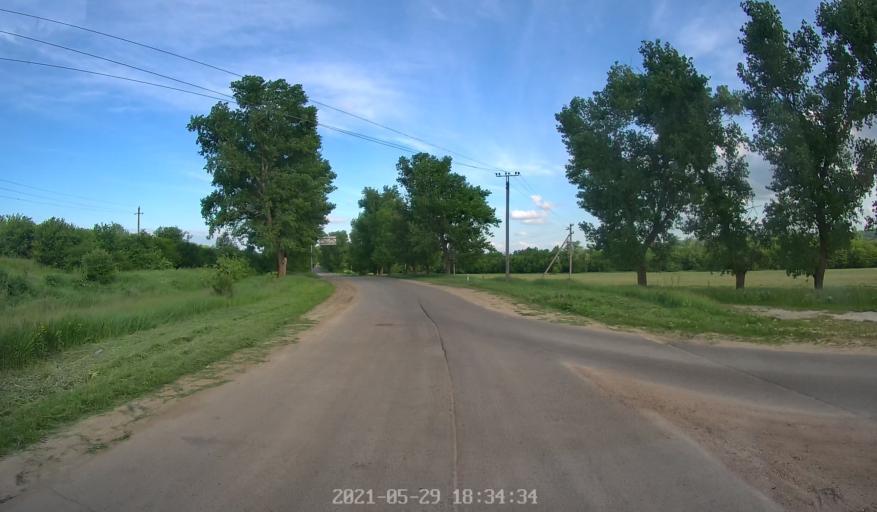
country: MD
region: Chisinau
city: Singera
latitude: 46.8125
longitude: 28.9132
